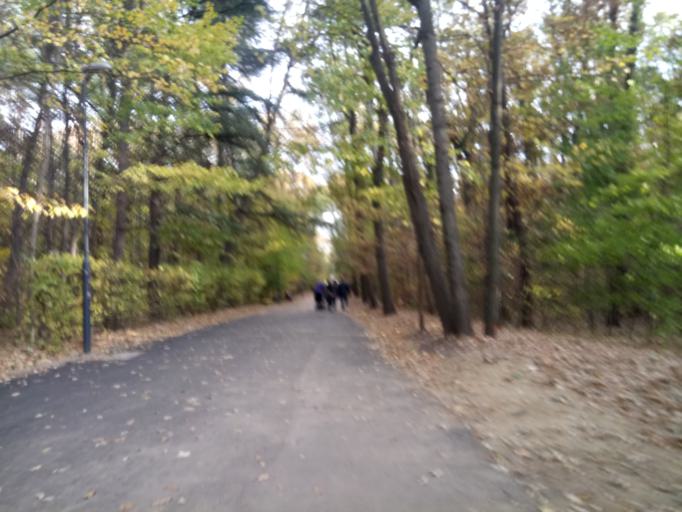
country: BG
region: Sofia-Capital
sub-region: Stolichna Obshtina
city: Sofia
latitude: 42.6766
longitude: 23.3478
